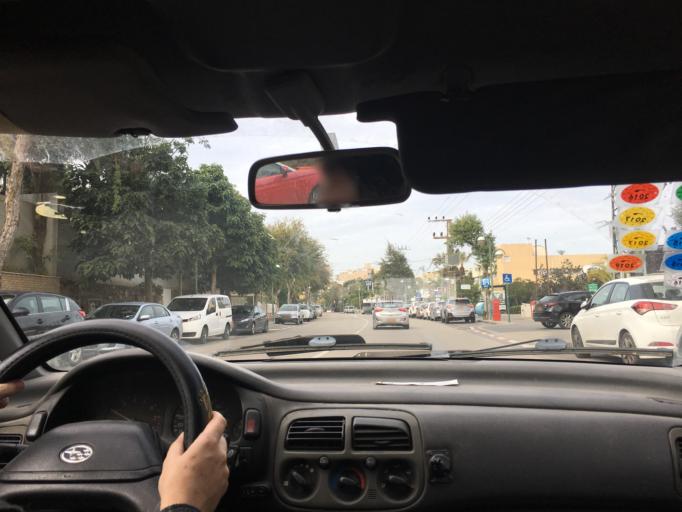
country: IL
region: Tel Aviv
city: Ramat HaSharon
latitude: 32.1360
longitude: 34.8451
